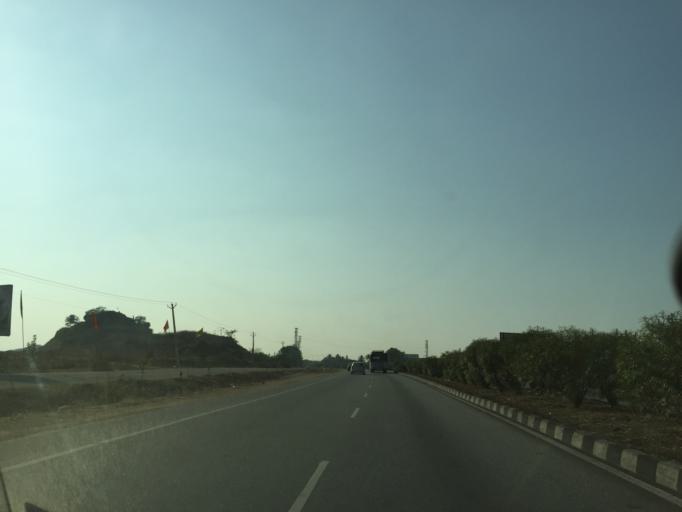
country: IN
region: Telangana
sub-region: Nalgonda
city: Bhongir
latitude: 17.5040
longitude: 78.8710
